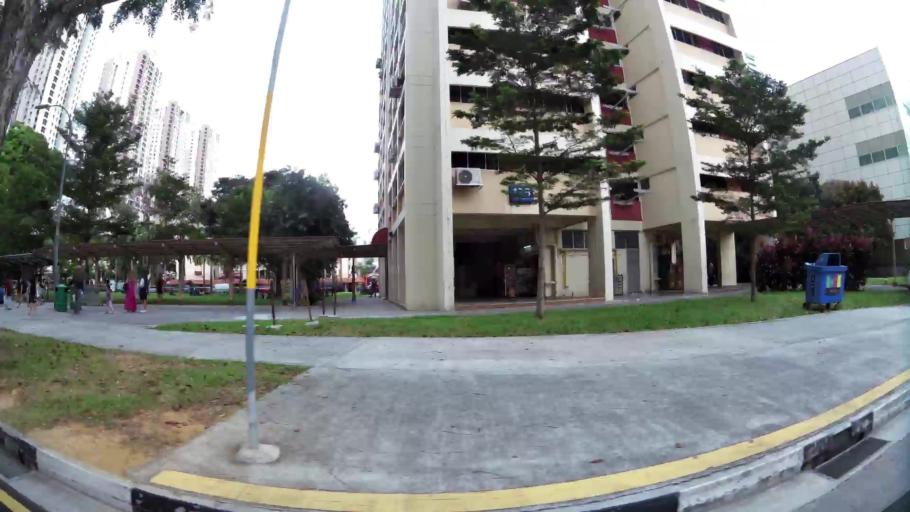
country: SG
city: Singapore
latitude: 1.3334
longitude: 103.8468
